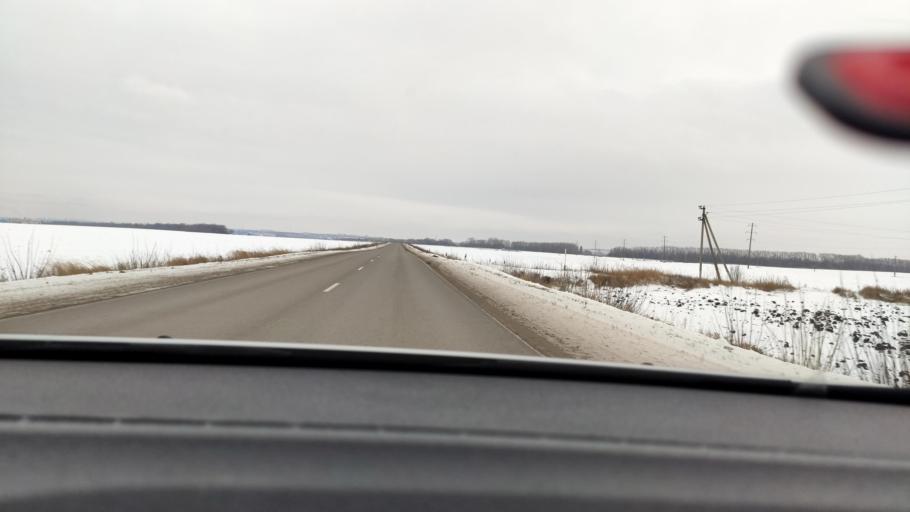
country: RU
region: Voronezj
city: Latnaya
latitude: 51.7422
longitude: 38.9405
